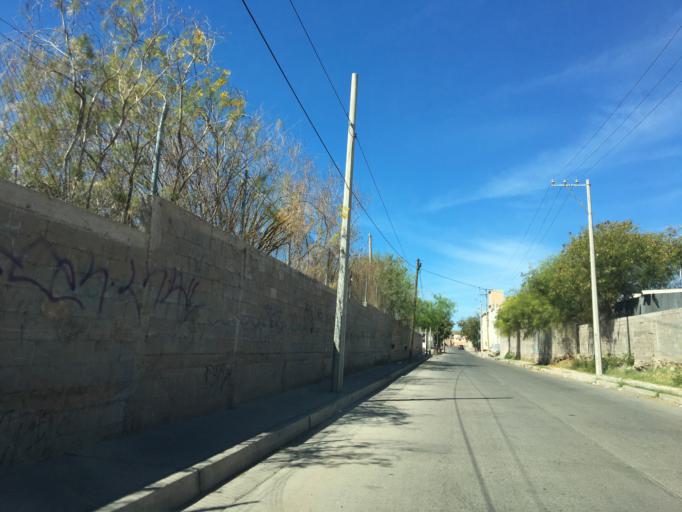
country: MX
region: Sonora
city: Heroica Guaymas
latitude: 27.9246
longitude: -110.9137
